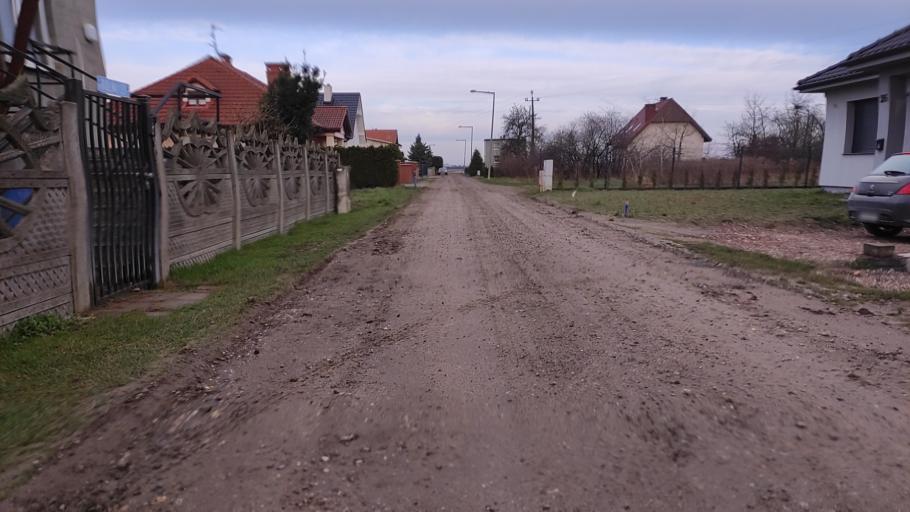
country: PL
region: Greater Poland Voivodeship
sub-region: Powiat poznanski
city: Kleszczewo
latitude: 52.4007
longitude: 17.1537
